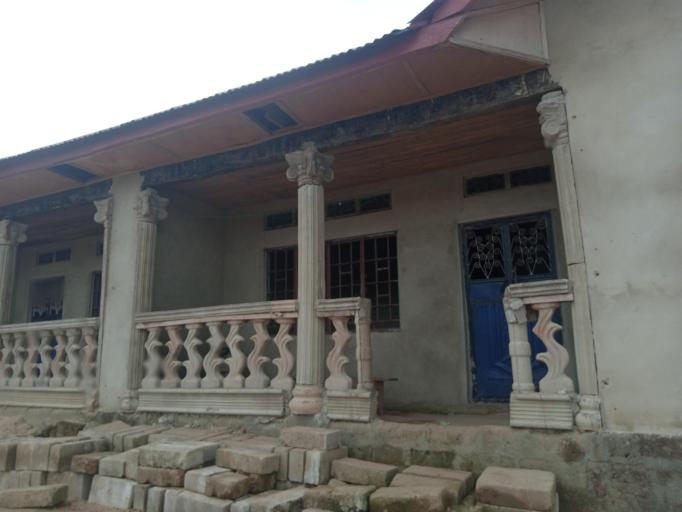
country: SL
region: Southern Province
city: Bo
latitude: 7.9838
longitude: -11.7464
